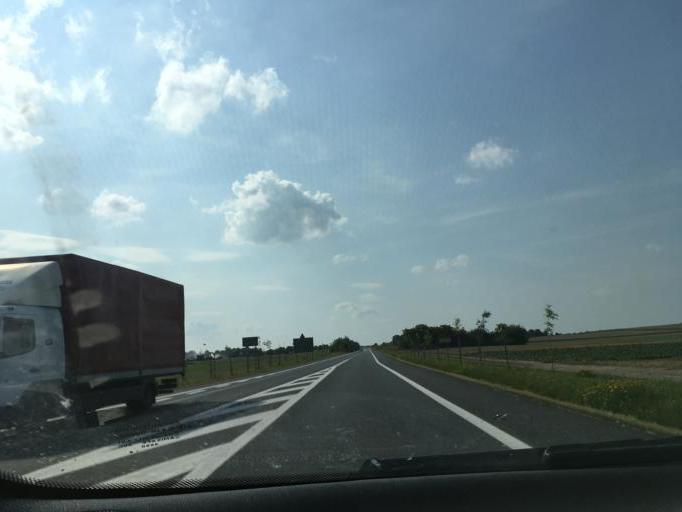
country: PL
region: Opole Voivodeship
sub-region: Powiat prudnicki
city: Prudnik
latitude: 50.3350
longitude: 17.5862
